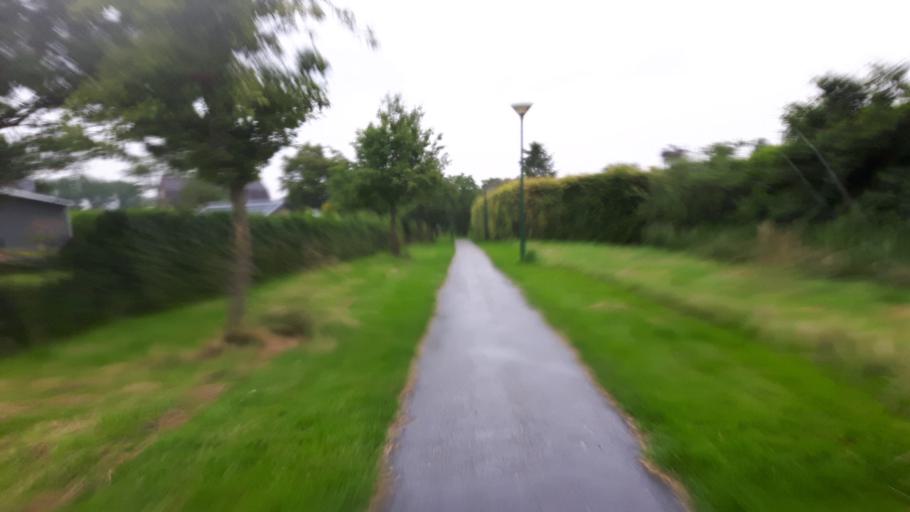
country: NL
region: Utrecht
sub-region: Gemeente Lopik
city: Lopik
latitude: 51.9831
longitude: 5.0009
